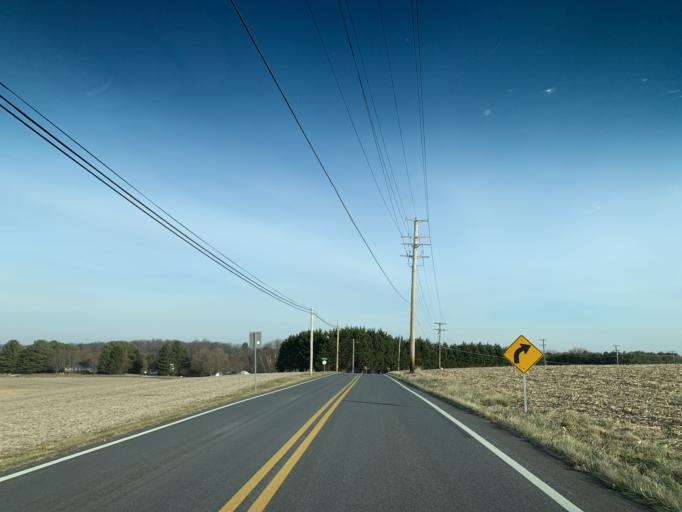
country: US
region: Maryland
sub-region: Carroll County
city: Hampstead
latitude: 39.6115
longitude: -76.8208
